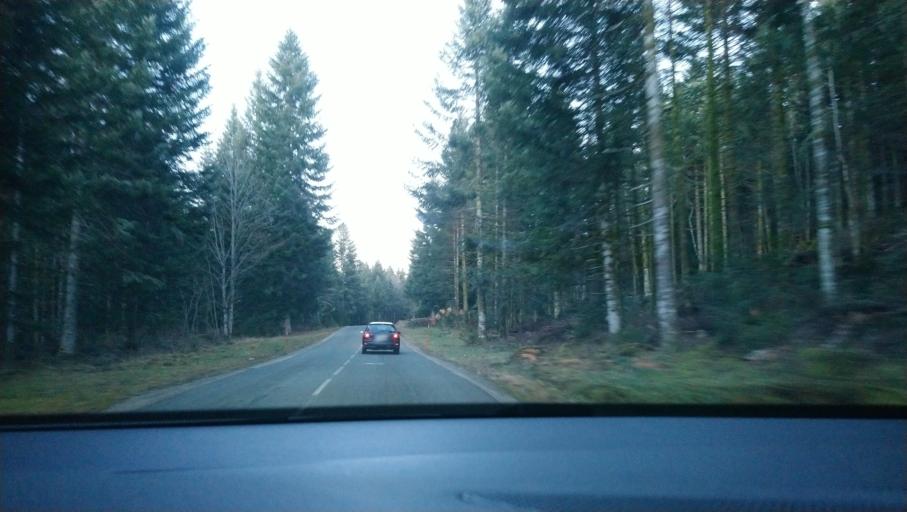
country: FR
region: Franche-Comte
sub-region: Departement du Doubs
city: Jougne
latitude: 46.8093
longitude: 6.2786
